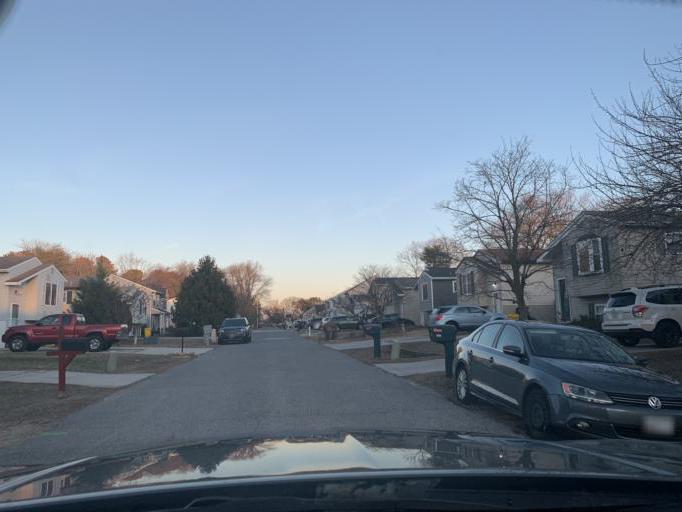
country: US
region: Maryland
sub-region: Anne Arundel County
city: Glen Burnie
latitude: 39.1549
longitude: -76.6412
